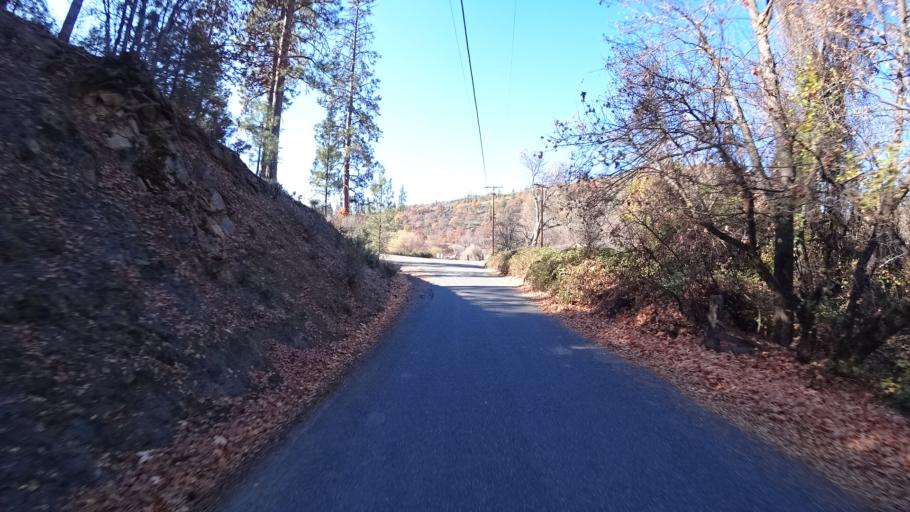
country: US
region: California
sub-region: Siskiyou County
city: Yreka
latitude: 41.8303
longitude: -122.8459
